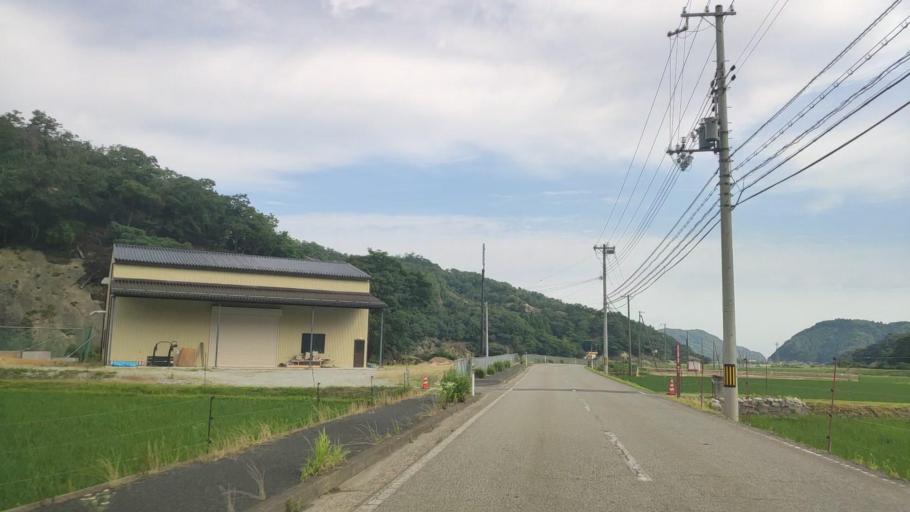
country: JP
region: Hyogo
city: Toyooka
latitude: 35.6202
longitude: 134.8418
